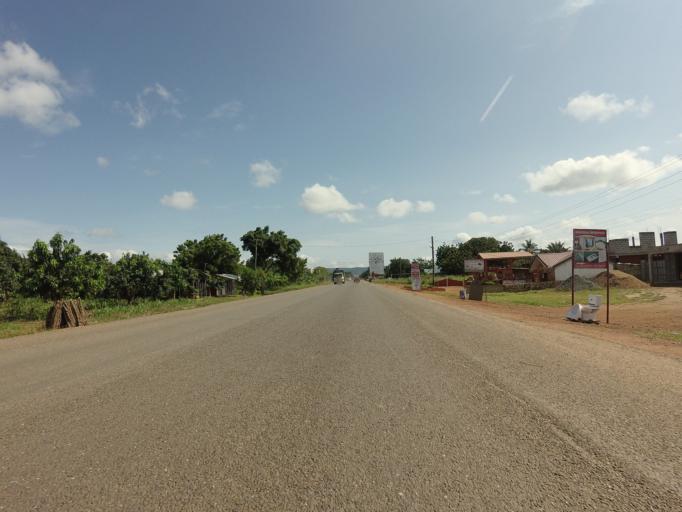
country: GH
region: Eastern
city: Aburi
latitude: 5.8319
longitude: -0.1178
